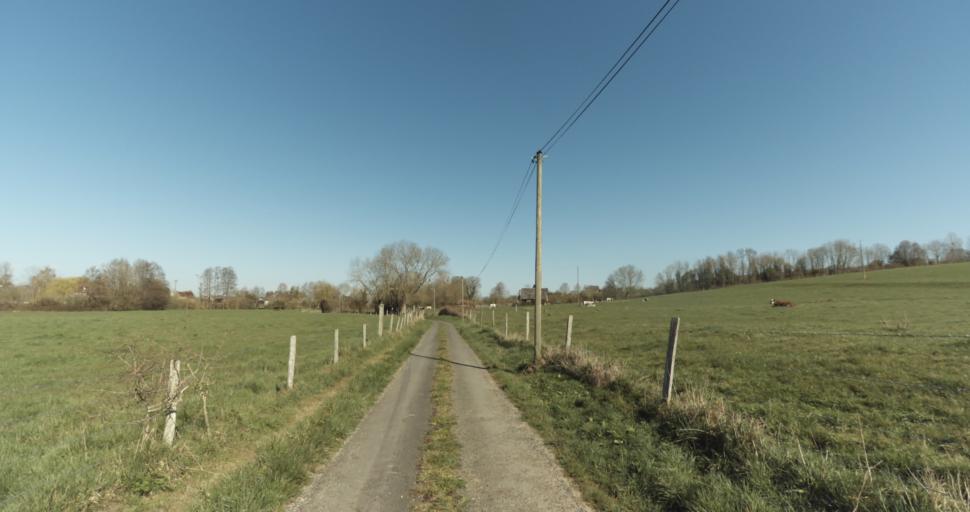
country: FR
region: Lower Normandy
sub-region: Departement du Calvados
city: Saint-Pierre-sur-Dives
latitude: 48.9870
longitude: 0.0332
